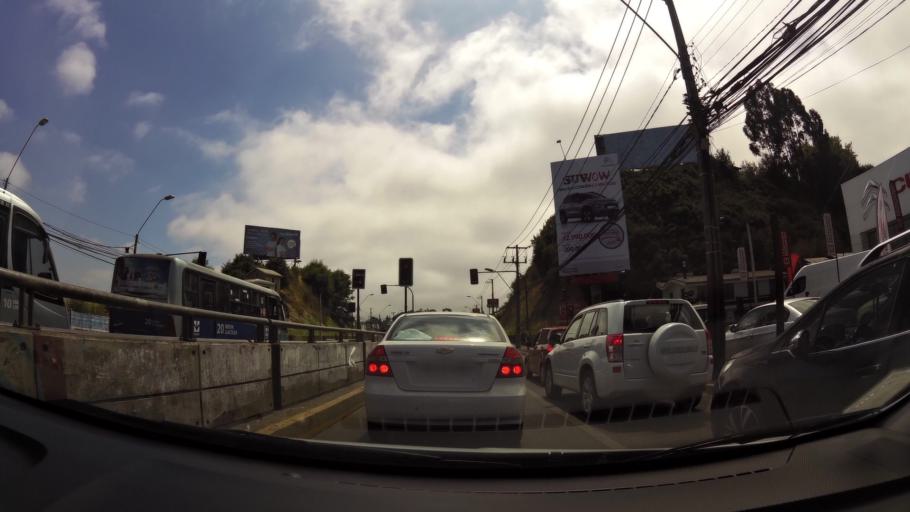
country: CL
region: Biobio
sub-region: Provincia de Concepcion
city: Concepcion
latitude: -36.8042
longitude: -73.0545
